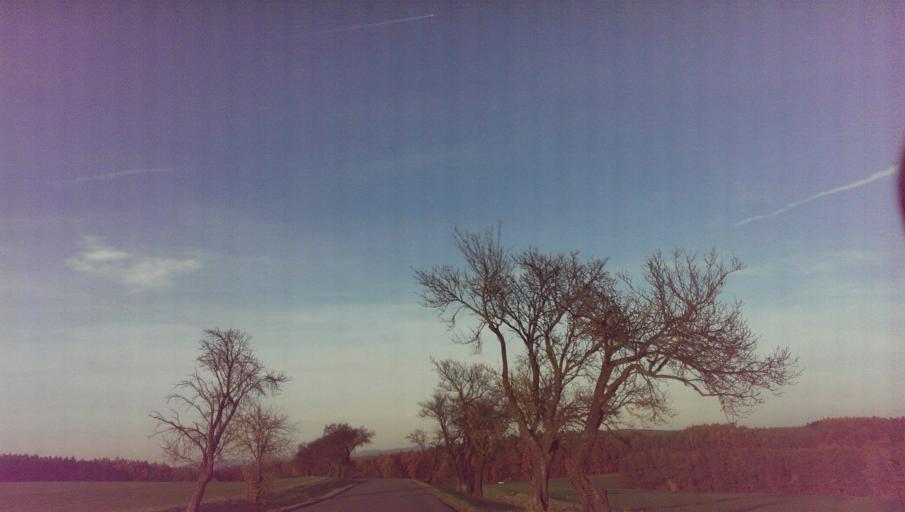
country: CZ
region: Zlin
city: Tecovice
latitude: 49.1776
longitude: 17.6058
